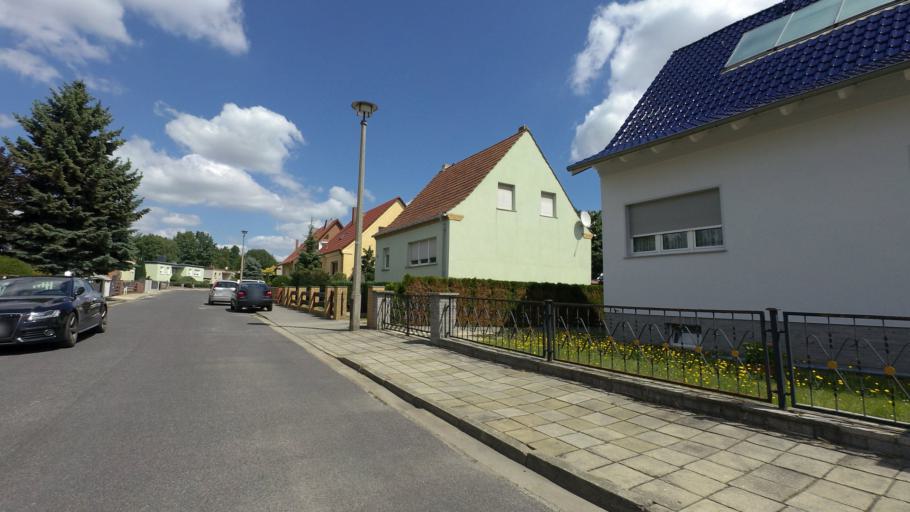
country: DE
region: Brandenburg
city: Finsterwalde
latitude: 51.6421
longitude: 13.6927
